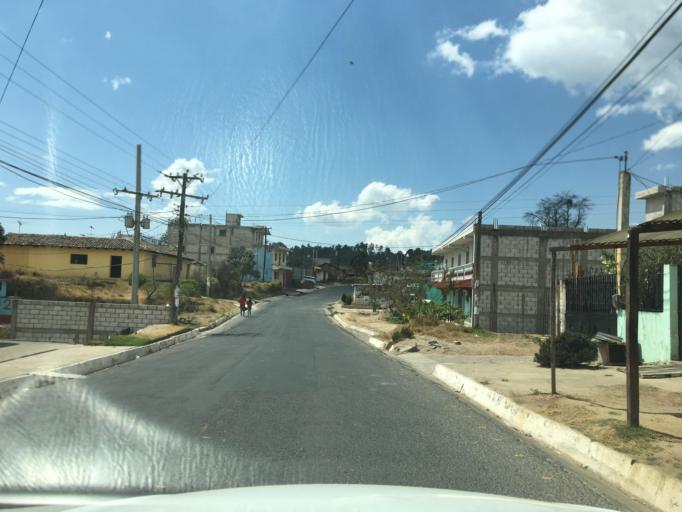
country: GT
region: Totonicapan
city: San Cristobal Totonicapan
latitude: 14.9074
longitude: -91.4540
